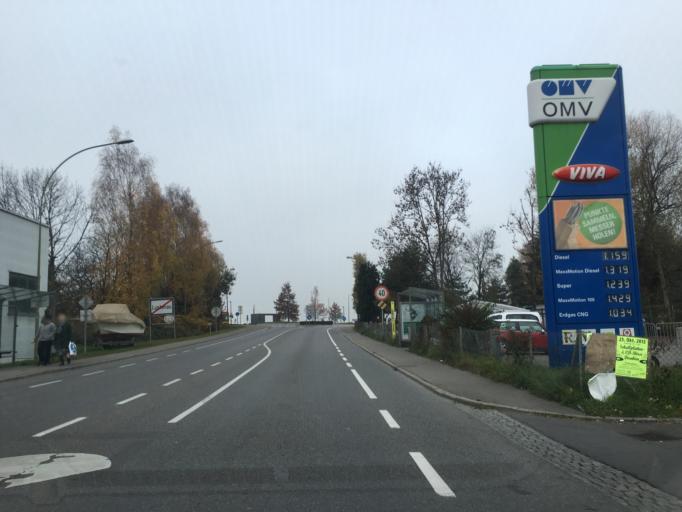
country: AT
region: Vorarlberg
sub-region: Politischer Bezirk Dornbirn
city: Lustenau
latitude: 47.4496
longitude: 9.6645
